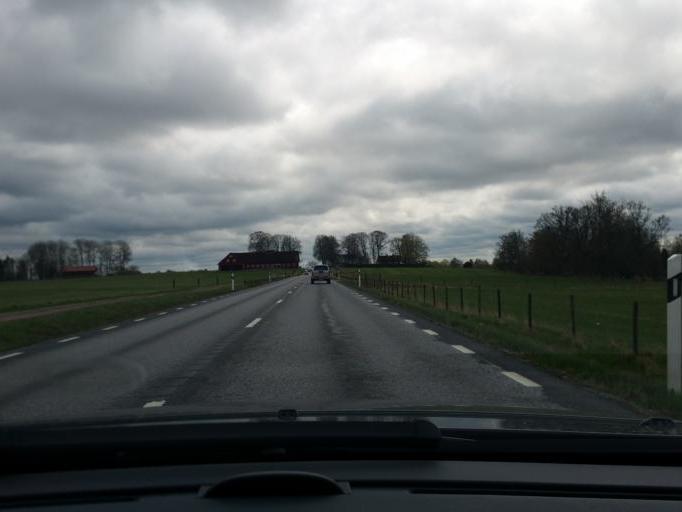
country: SE
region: Kronoberg
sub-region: Vaxjo Kommun
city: Ingelstad
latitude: 56.7788
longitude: 14.9078
